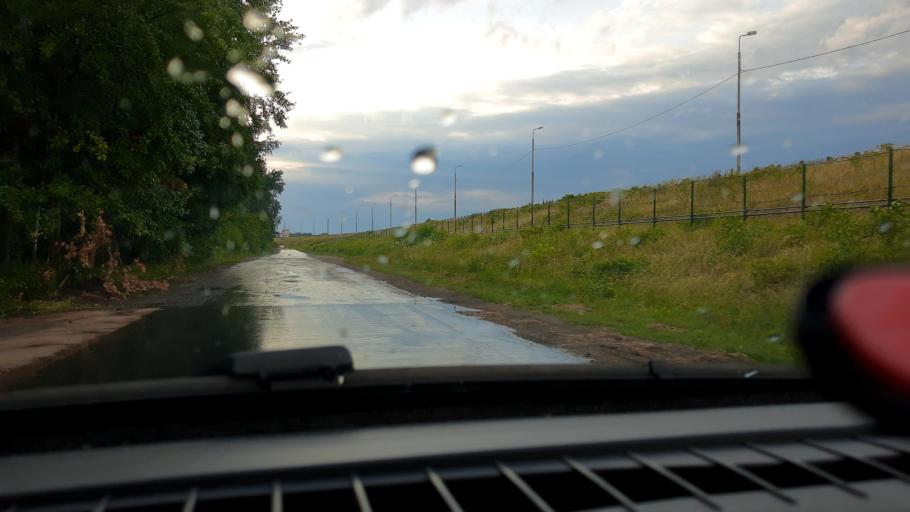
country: RU
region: Nizjnij Novgorod
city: Gorodets
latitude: 56.6671
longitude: 43.4308
